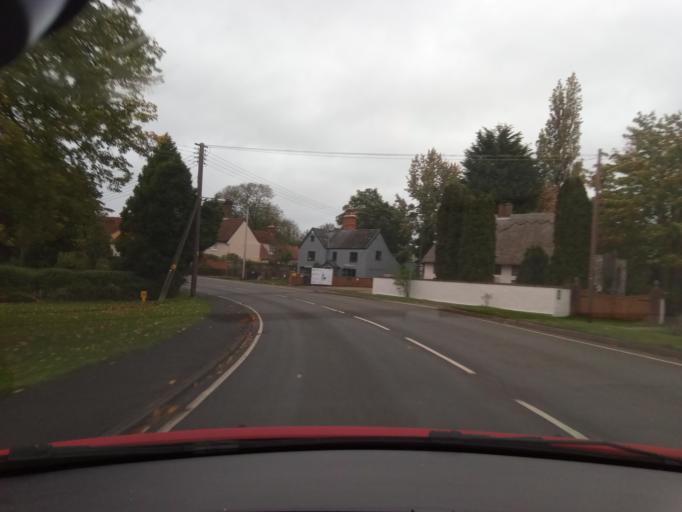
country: GB
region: England
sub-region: Essex
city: Great Yeldham
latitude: 52.0394
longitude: 0.5319
